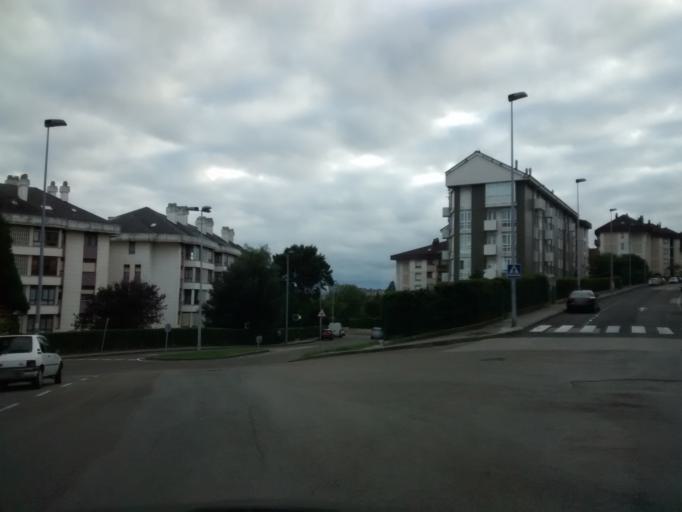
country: ES
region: Cantabria
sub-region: Provincia de Cantabria
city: Santander
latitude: 43.4792
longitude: -3.7988
